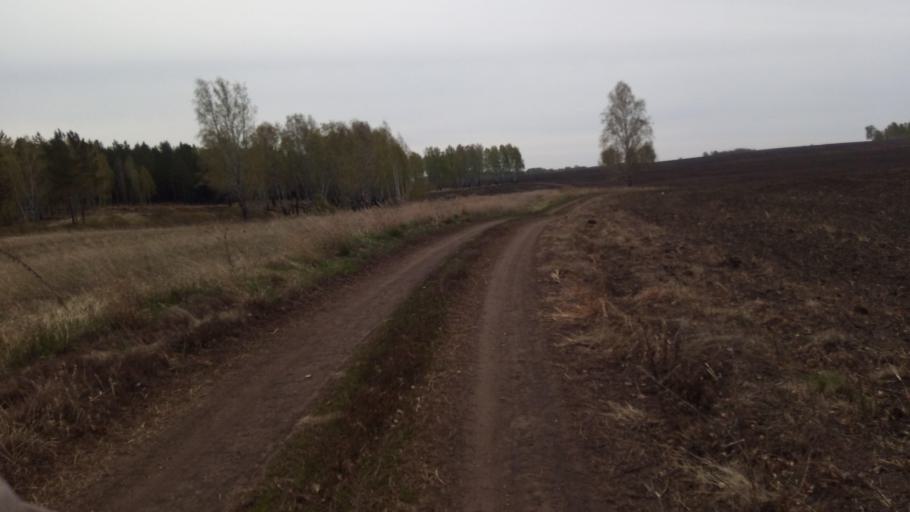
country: RU
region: Chelyabinsk
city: Timiryazevskiy
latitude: 55.0227
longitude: 60.8516
